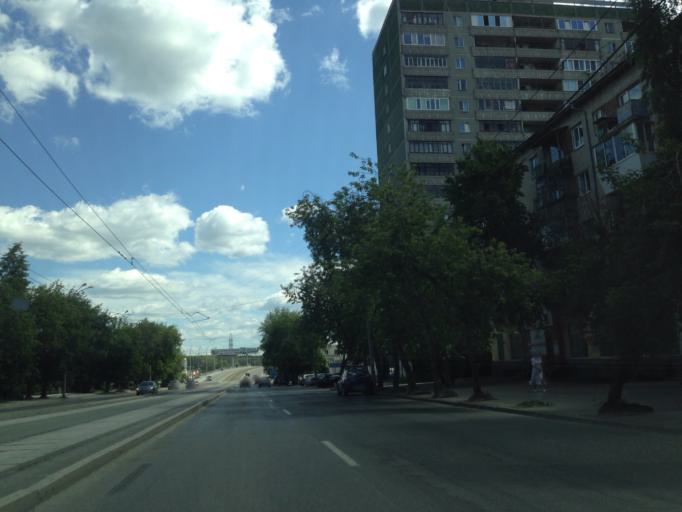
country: RU
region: Sverdlovsk
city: Yekaterinburg
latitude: 56.8411
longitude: 60.6605
